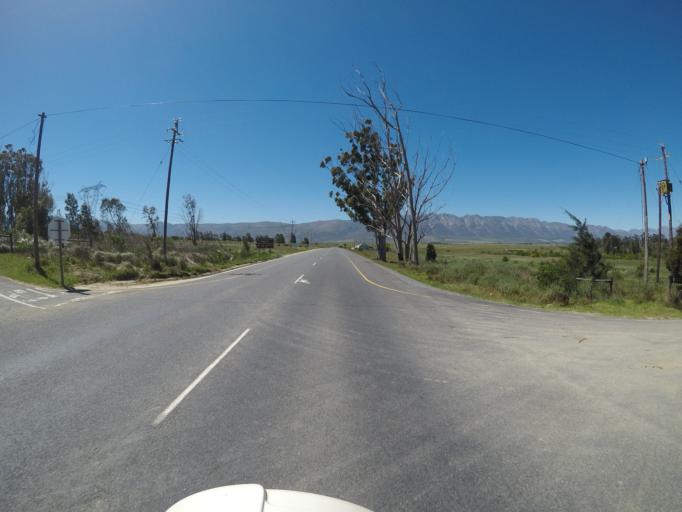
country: ZA
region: Western Cape
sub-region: Cape Winelands District Municipality
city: Ceres
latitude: -33.3095
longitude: 19.1040
